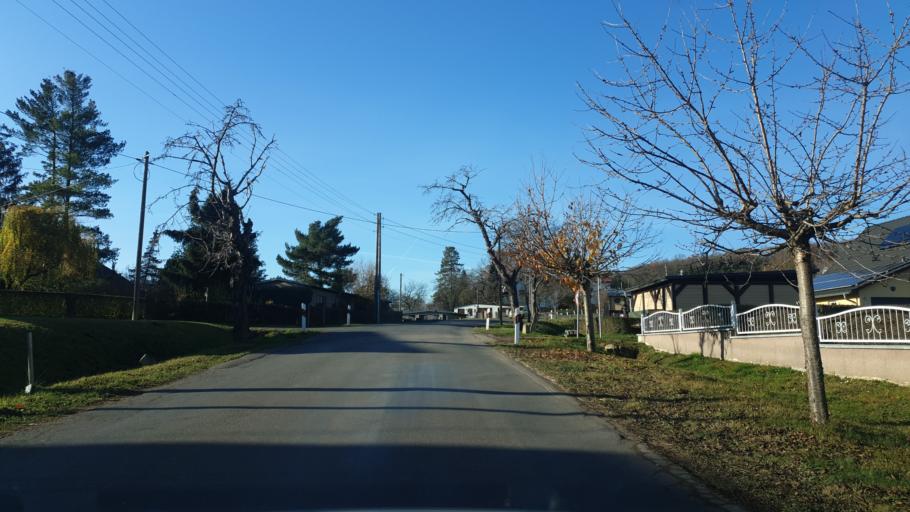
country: DE
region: Saxony-Anhalt
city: Wetterzeube
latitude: 51.0082
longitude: 12.0083
